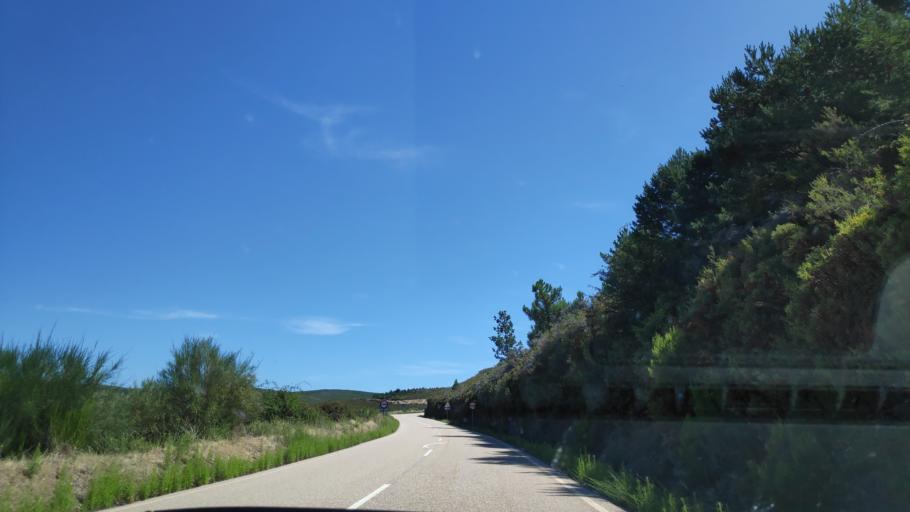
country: ES
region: Castille and Leon
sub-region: Provincia de Zamora
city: Requejo
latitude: 41.9926
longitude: -6.7021
